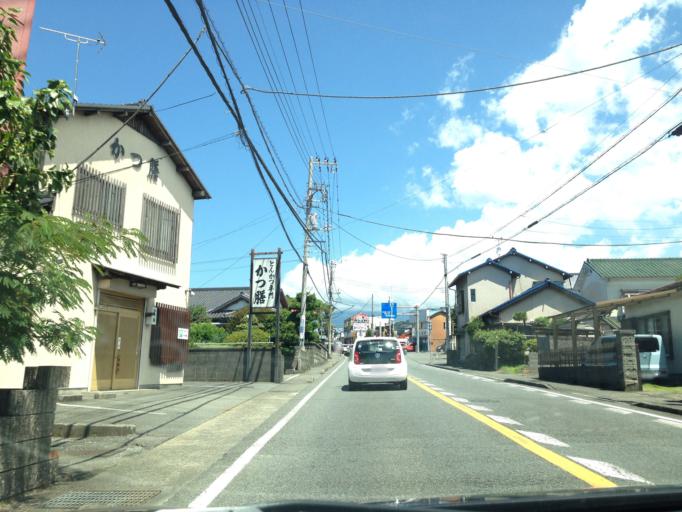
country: JP
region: Shizuoka
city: Fuji
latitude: 35.1677
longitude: 138.6891
